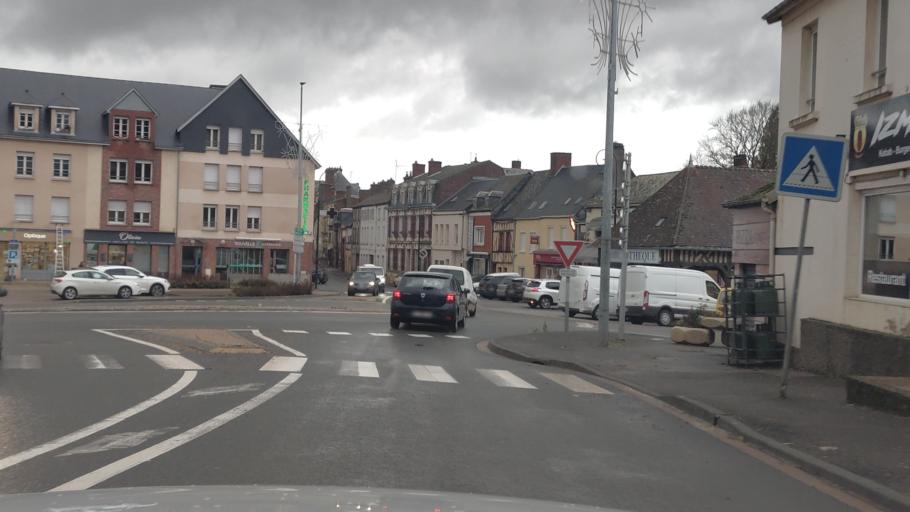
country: FR
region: Picardie
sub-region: Departement de l'Oise
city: Saint-Omer-en-Chaussee
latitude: 49.5737
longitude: 1.9564
